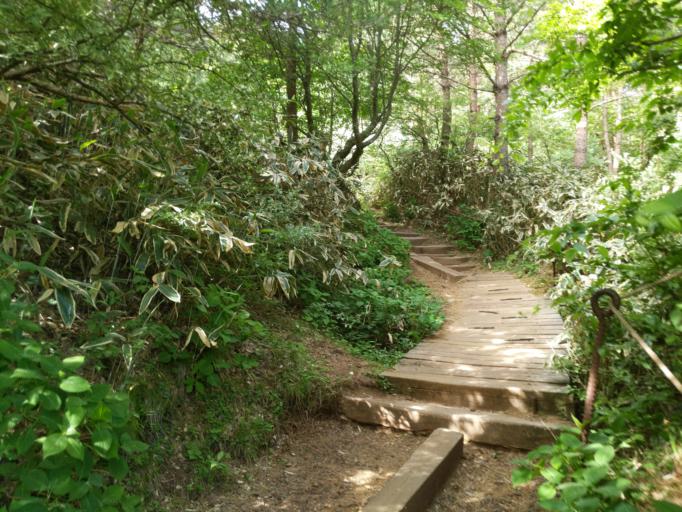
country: KR
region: Jeju-do
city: Jeju-si
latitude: 33.3817
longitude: 126.5340
